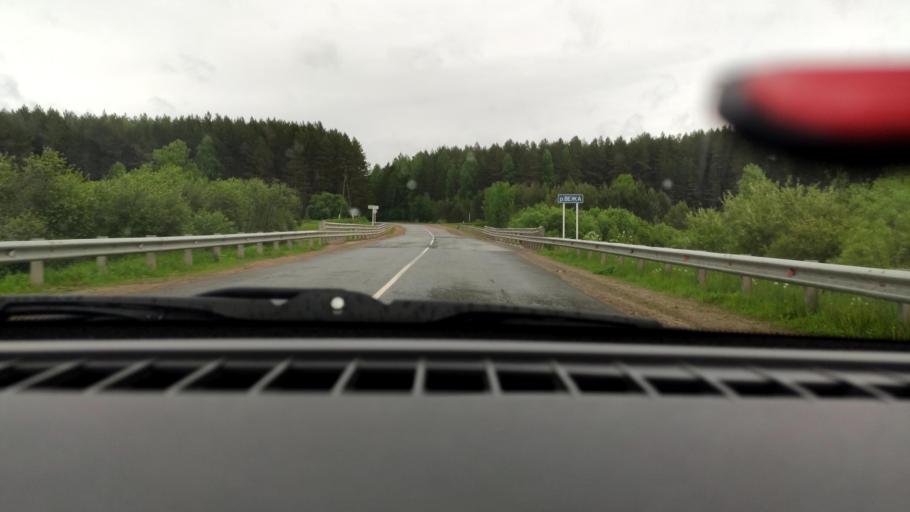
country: RU
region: Perm
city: Karagay
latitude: 58.2537
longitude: 54.8727
